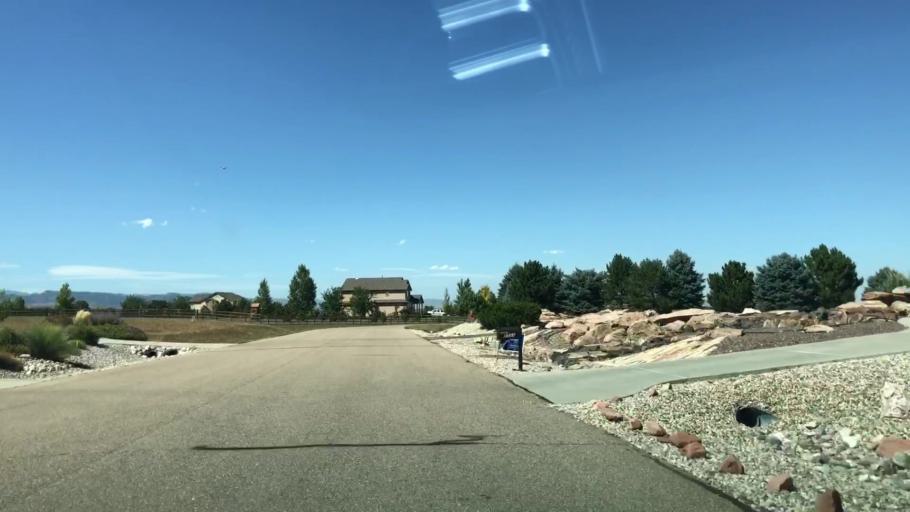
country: US
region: Colorado
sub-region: Weld County
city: Windsor
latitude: 40.4456
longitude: -104.9579
